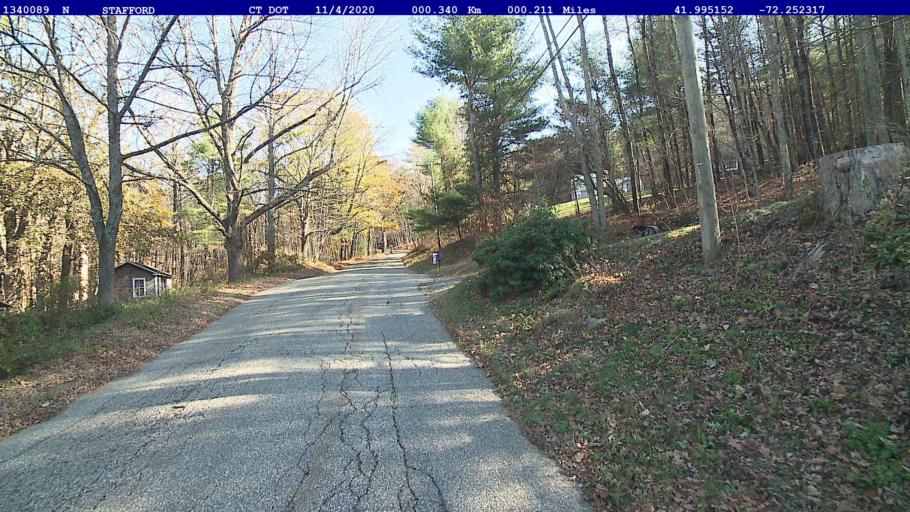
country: US
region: Connecticut
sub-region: Tolland County
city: Stafford
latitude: 41.9952
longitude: -72.2523
